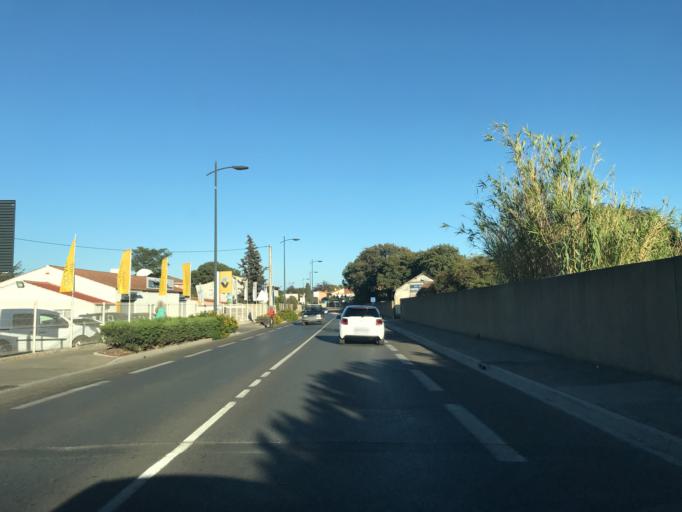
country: FR
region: Provence-Alpes-Cote d'Azur
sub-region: Departement du Var
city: Six-Fours-les-Plages
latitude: 43.0847
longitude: 5.8594
